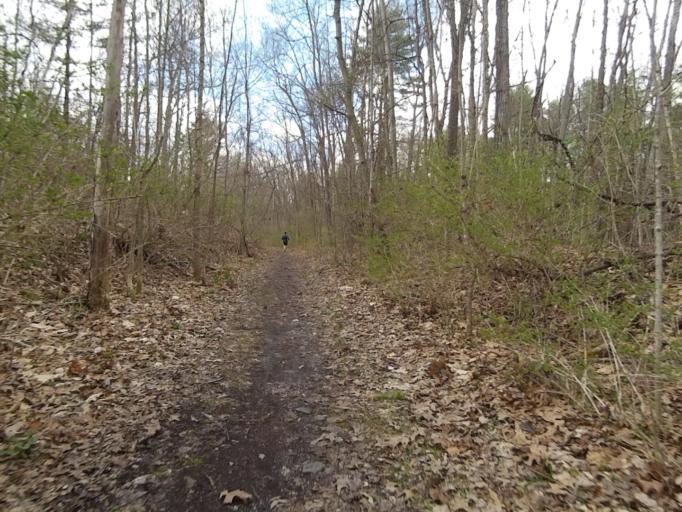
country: US
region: Pennsylvania
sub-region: Centre County
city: Park Forest Village
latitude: 40.8236
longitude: -77.9251
